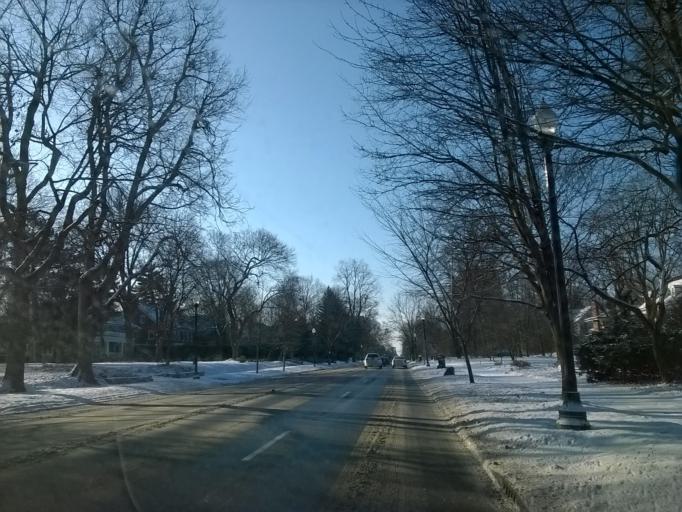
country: US
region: Indiana
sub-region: Marion County
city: Broad Ripple
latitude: 39.8321
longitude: -86.1570
